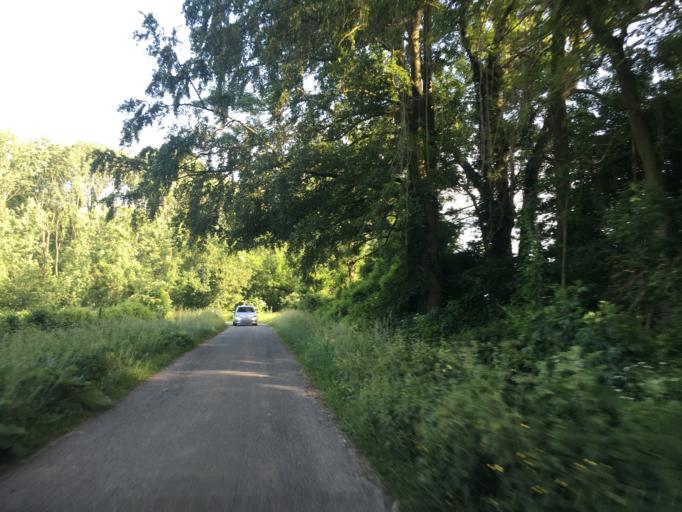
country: DE
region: North Rhine-Westphalia
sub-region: Regierungsbezirk Munster
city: Altenberge
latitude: 52.0155
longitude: 7.5320
